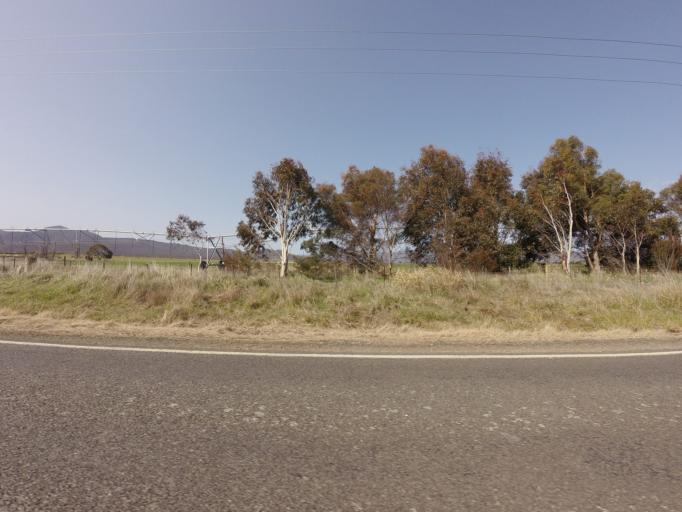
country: AU
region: Tasmania
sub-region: Northern Midlands
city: Evandale
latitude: -41.7876
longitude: 147.7148
